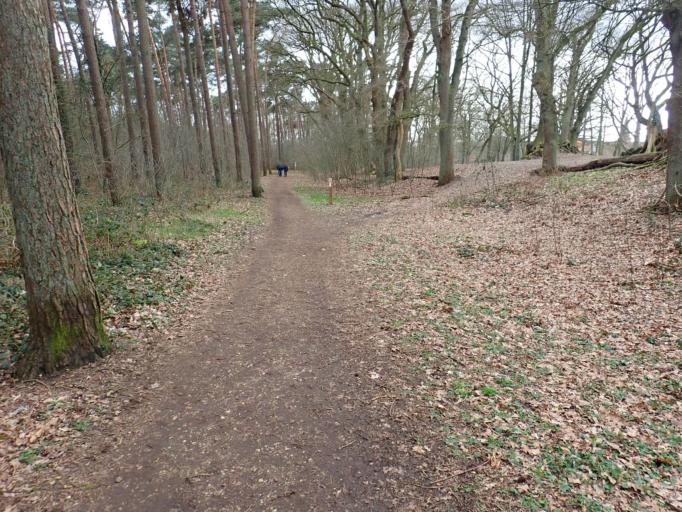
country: BE
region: Flanders
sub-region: Provincie Antwerpen
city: Schilde
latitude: 51.2947
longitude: 4.5888
